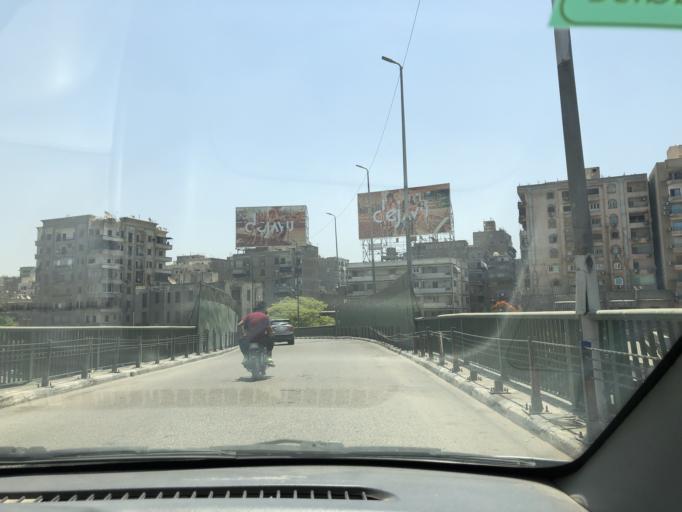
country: EG
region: Muhafazat al Qahirah
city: Cairo
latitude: 30.0671
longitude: 31.2592
